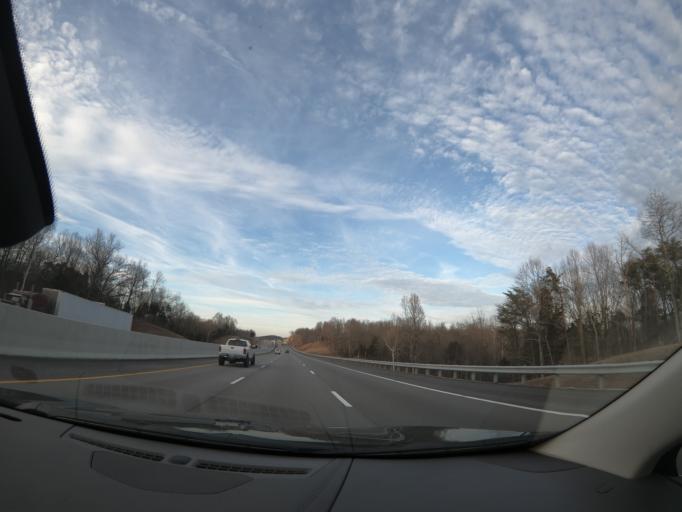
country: US
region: Kentucky
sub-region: Hart County
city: Munfordville
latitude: 37.3977
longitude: -85.8824
